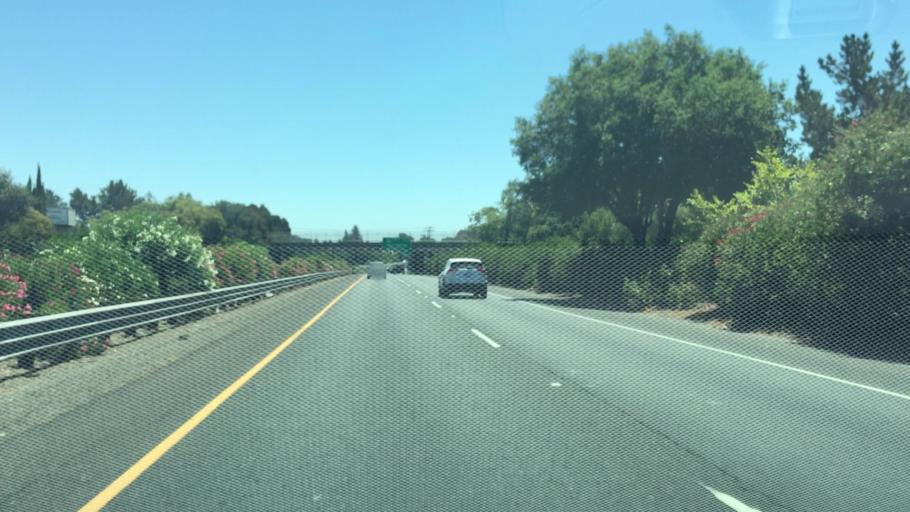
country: US
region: California
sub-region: Napa County
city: Napa
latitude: 38.2893
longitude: -122.3016
